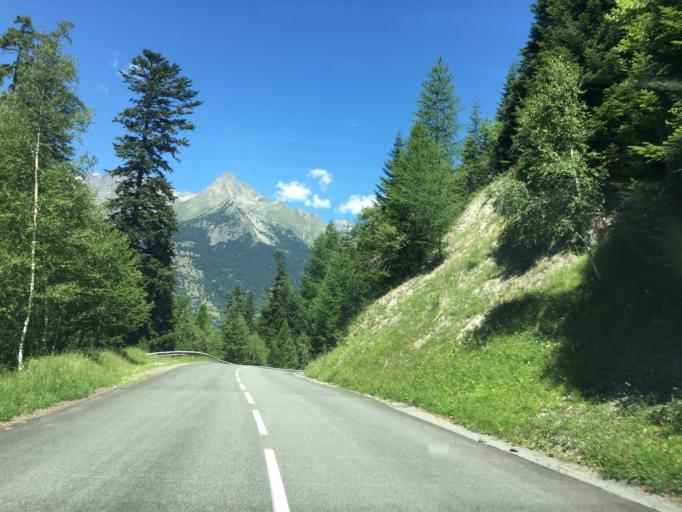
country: FR
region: Rhone-Alpes
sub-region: Departement de la Savoie
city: Modane
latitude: 45.1840
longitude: 6.6590
